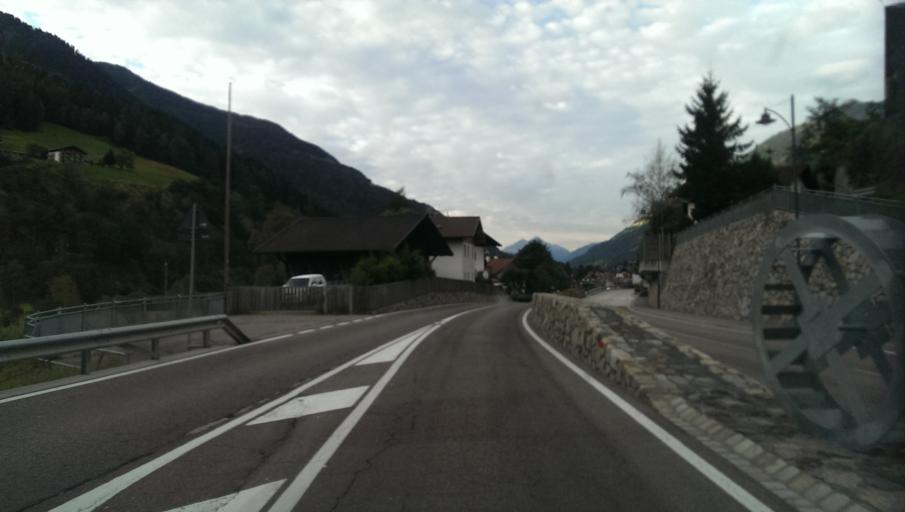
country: IT
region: Trentino-Alto Adige
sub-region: Bolzano
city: San Martino in Passiria
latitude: 46.7867
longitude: 11.2309
